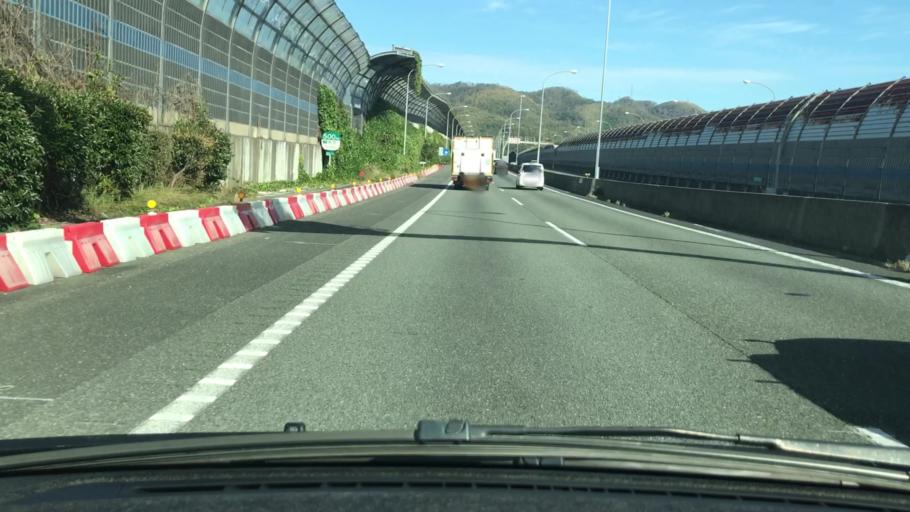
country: JP
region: Kyoto
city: Yawata
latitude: 34.8805
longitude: 135.6579
